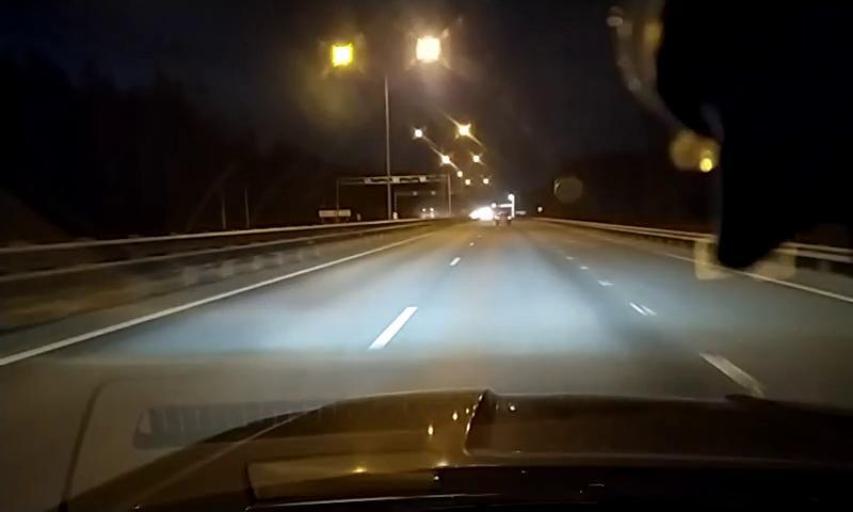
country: RU
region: Leningrad
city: Agalatovo
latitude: 60.2194
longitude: 30.3592
